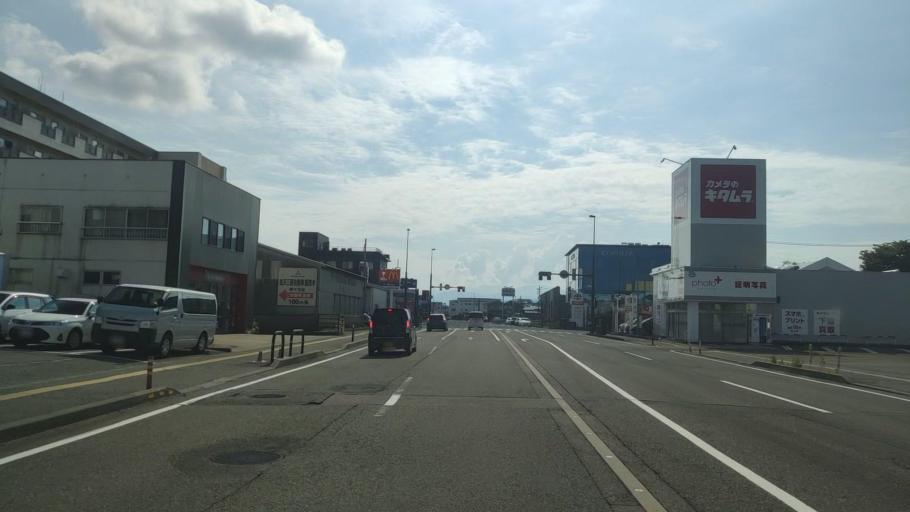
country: JP
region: Ishikawa
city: Nonoichi
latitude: 36.5323
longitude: 136.5998
